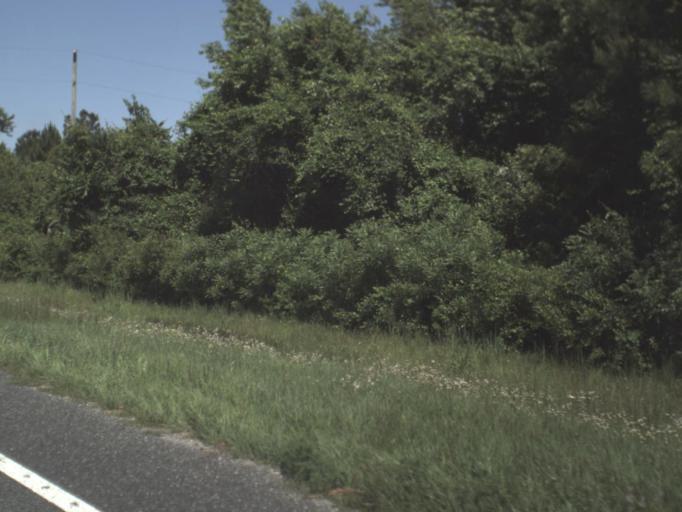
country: US
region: Florida
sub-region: Columbia County
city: Watertown
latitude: 30.2027
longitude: -82.4472
